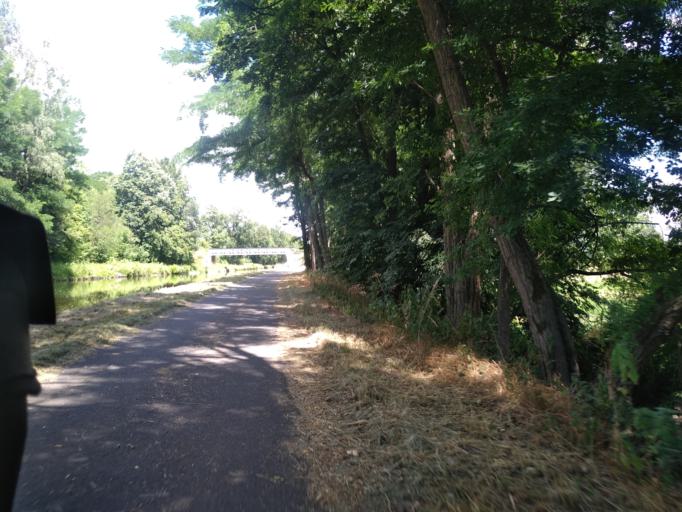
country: FR
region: Rhone-Alpes
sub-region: Departement de la Loire
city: Briennon
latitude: 46.1282
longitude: 4.0779
